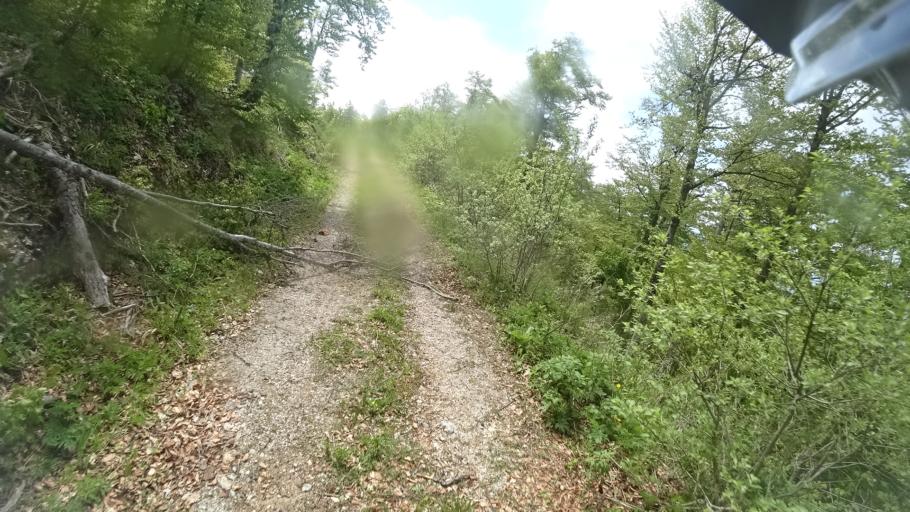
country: BA
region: Federation of Bosnia and Herzegovina
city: Orasac
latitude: 44.5703
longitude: 15.8724
